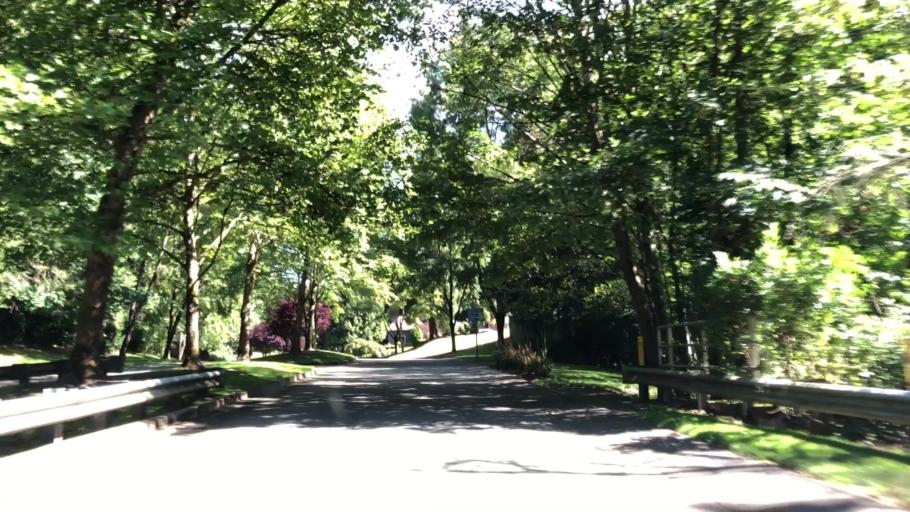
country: US
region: Washington
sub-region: King County
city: Cottage Lake
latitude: 47.7167
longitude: -122.0752
